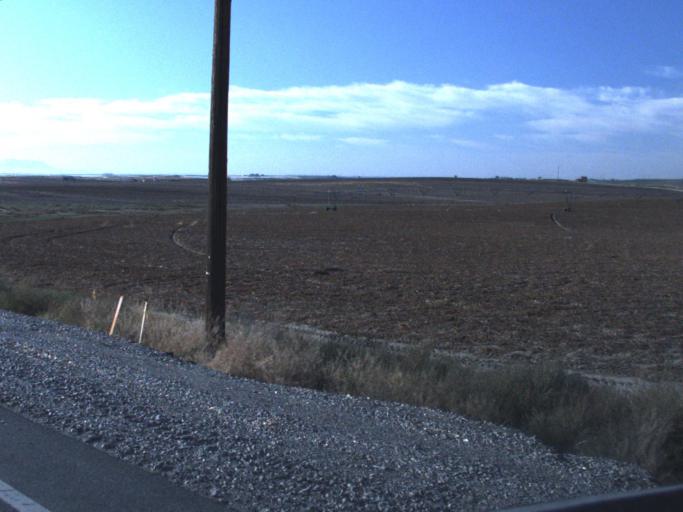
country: US
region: Washington
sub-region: Walla Walla County
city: Burbank
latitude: 46.2152
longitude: -118.9129
